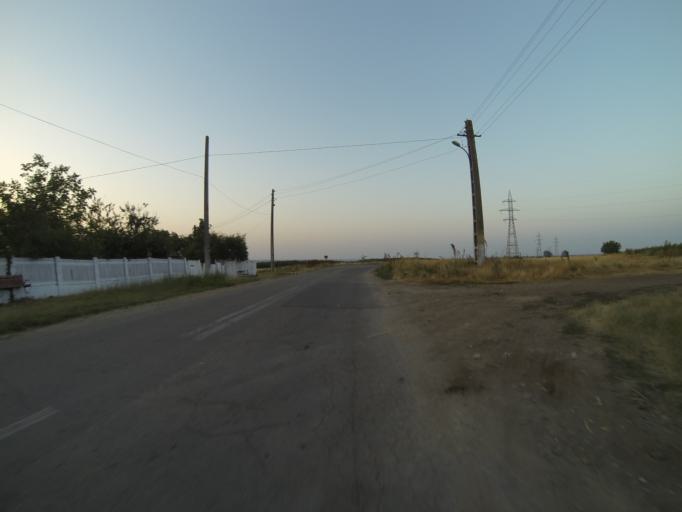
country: RO
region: Dolj
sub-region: Comuna Dranicu
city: Padea
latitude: 44.0145
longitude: 23.8730
